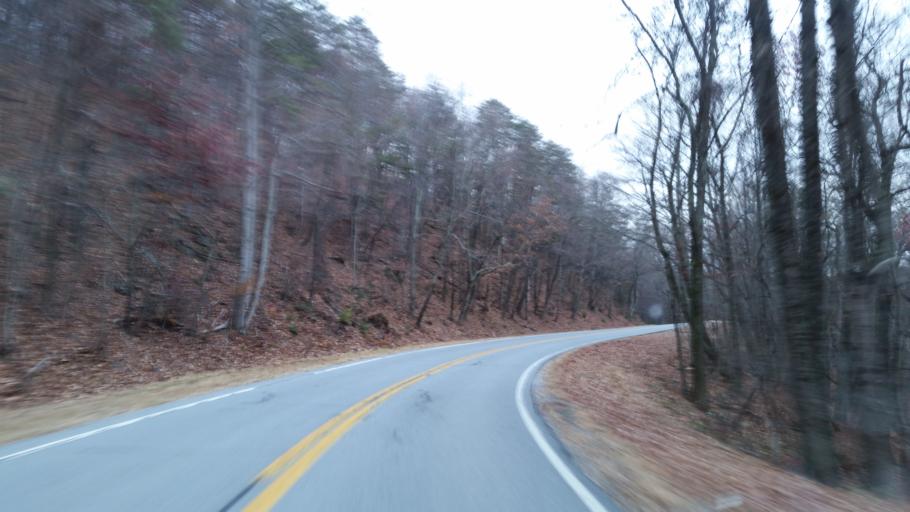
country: US
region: Georgia
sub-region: Pickens County
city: Jasper
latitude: 34.5424
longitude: -84.3161
